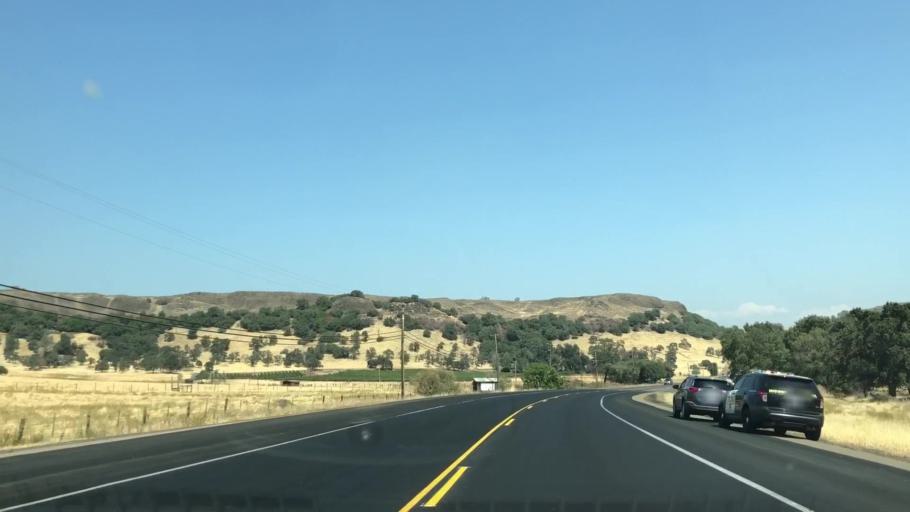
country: US
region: California
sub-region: Tuolumne County
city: Jamestown
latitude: 37.8872
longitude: -120.4969
